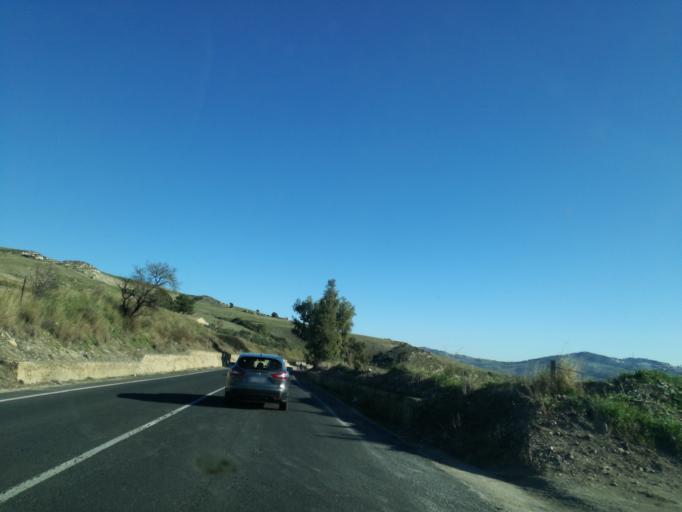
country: IT
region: Sicily
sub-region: Catania
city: San Michele di Ganzaria
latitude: 37.2291
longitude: 14.4395
